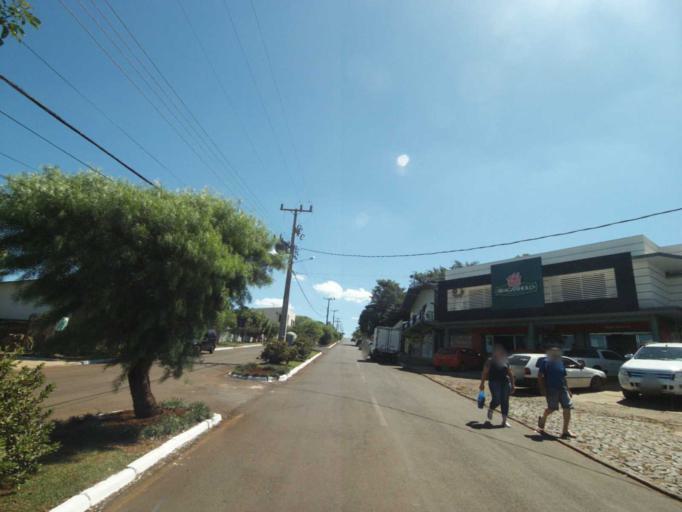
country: BR
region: Parana
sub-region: Laranjeiras Do Sul
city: Laranjeiras do Sul
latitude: -25.3821
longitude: -52.2050
